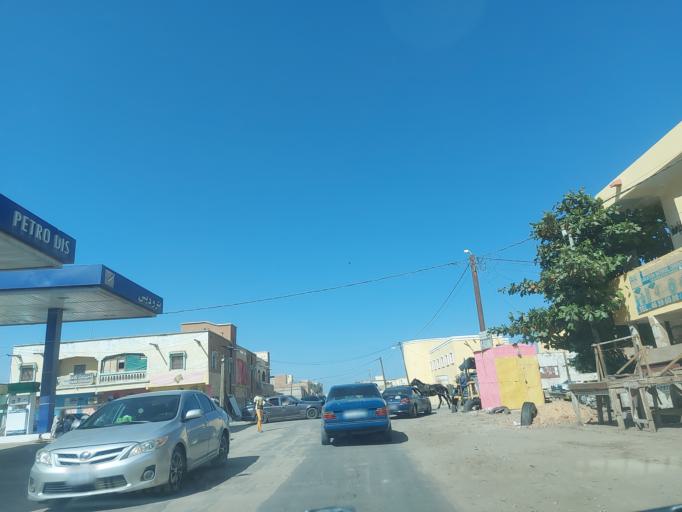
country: MR
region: Nouakchott
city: Nouakchott
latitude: 18.0750
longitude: -15.9981
